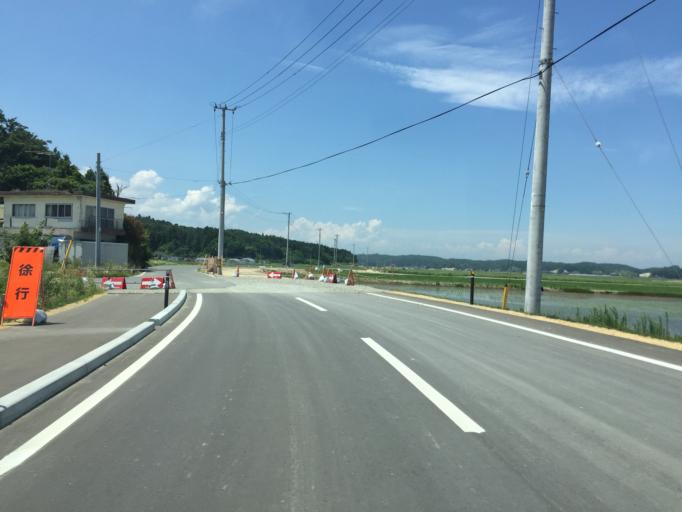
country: JP
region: Fukushima
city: Namie
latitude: 37.7217
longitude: 140.9974
